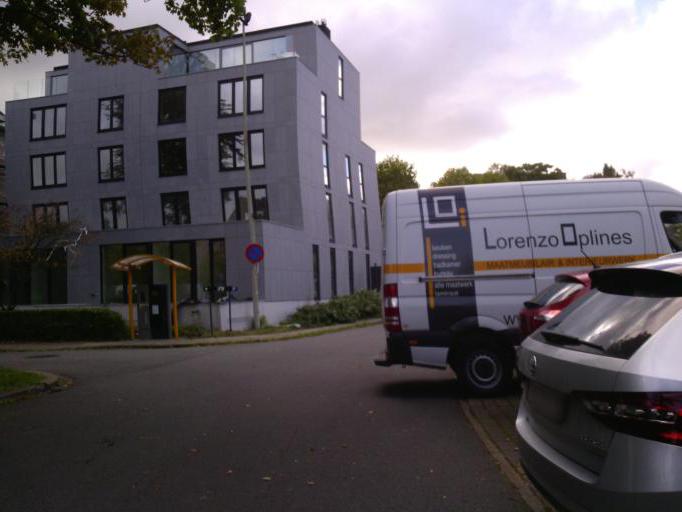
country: BE
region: Flanders
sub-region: Provincie West-Vlaanderen
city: Kortrijk
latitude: 50.8318
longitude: 3.2676
